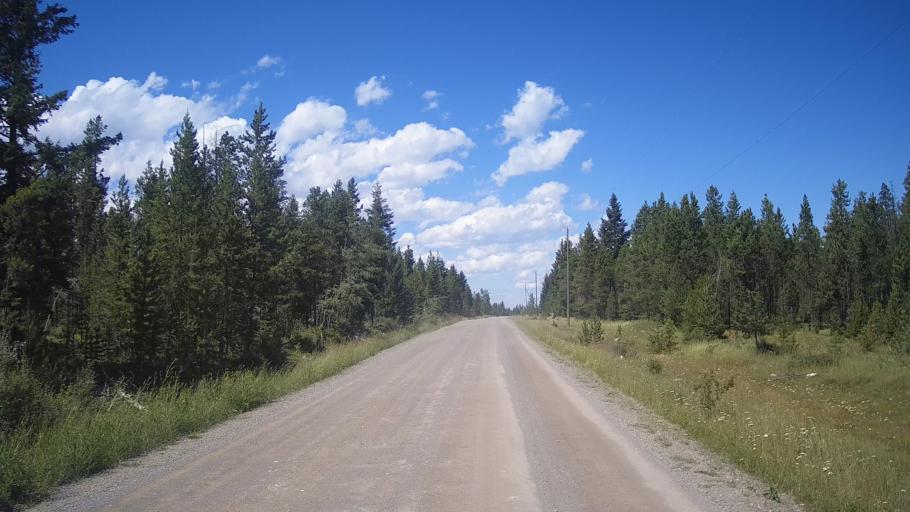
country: CA
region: British Columbia
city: Cache Creek
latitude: 51.2170
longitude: -121.6095
